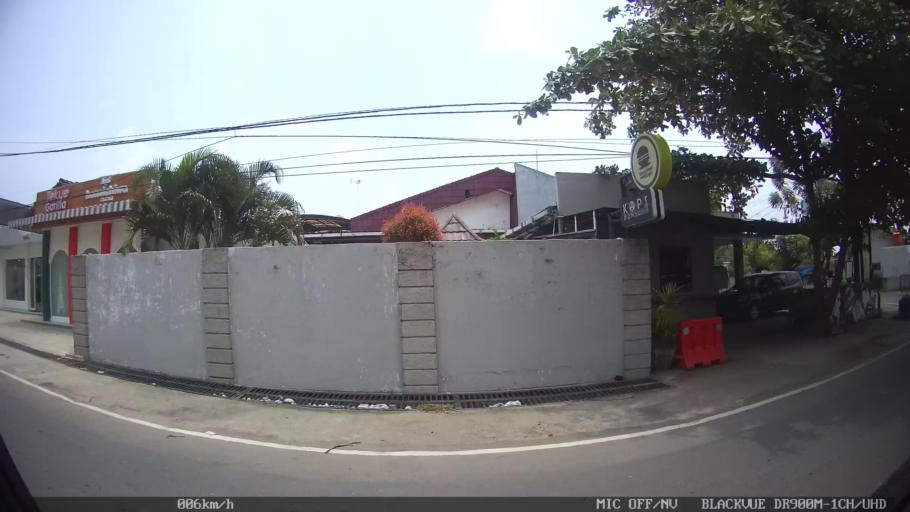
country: ID
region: Lampung
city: Bandarlampung
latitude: -5.4149
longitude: 105.2736
